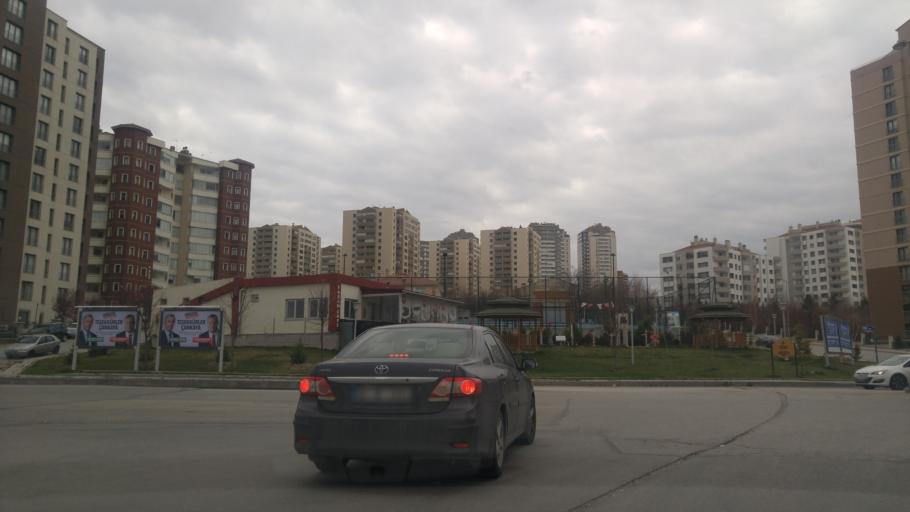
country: TR
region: Ankara
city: Etimesgut
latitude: 39.8663
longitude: 32.6407
